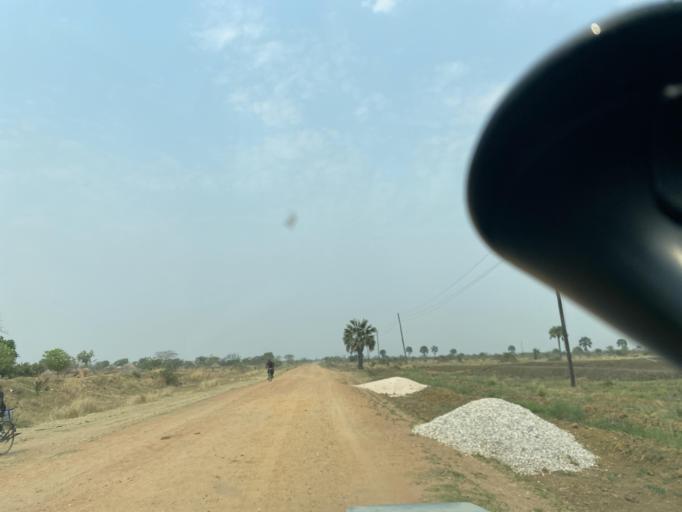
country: ZM
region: Lusaka
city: Kafue
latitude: -15.6742
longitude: 28.0164
